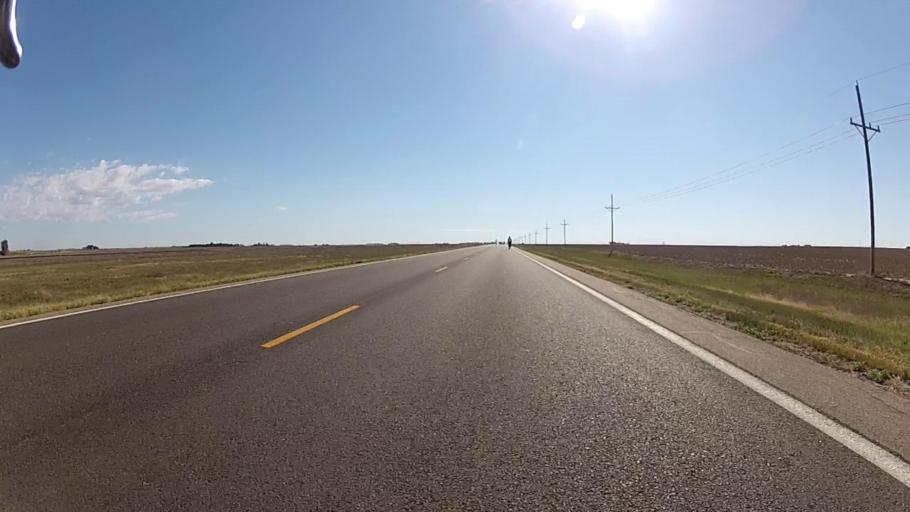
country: US
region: Kansas
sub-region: Gray County
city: Cimarron
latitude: 37.5793
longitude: -100.5137
